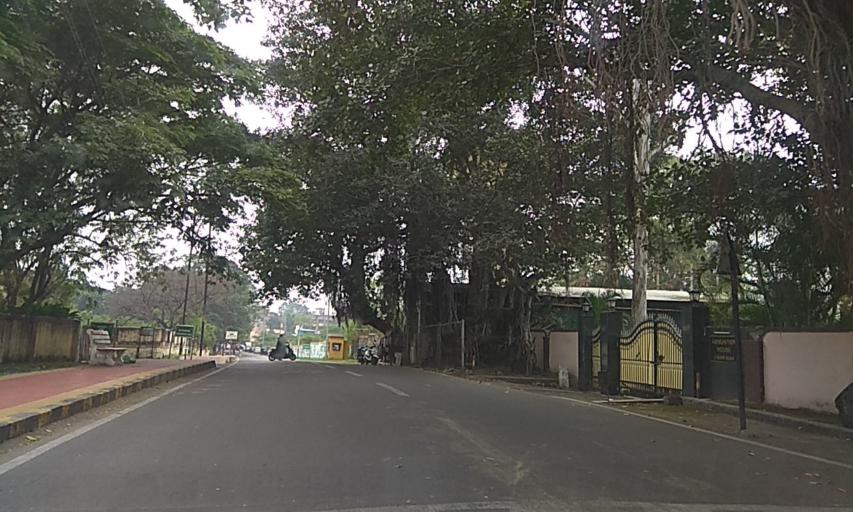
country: IN
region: Maharashtra
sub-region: Pune Division
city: Khadki
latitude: 18.5535
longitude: 73.8531
